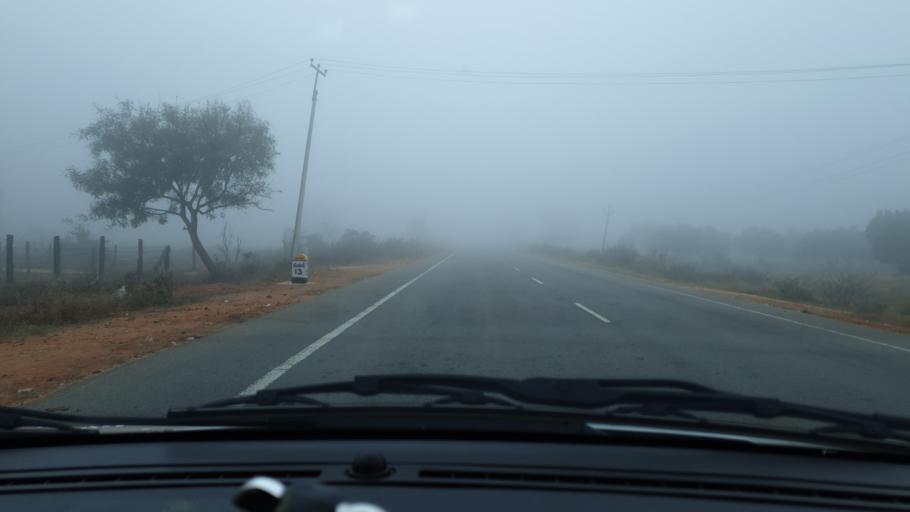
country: IN
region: Telangana
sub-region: Mahbubnagar
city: Nagar Karnul
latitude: 16.6874
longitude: 78.5226
